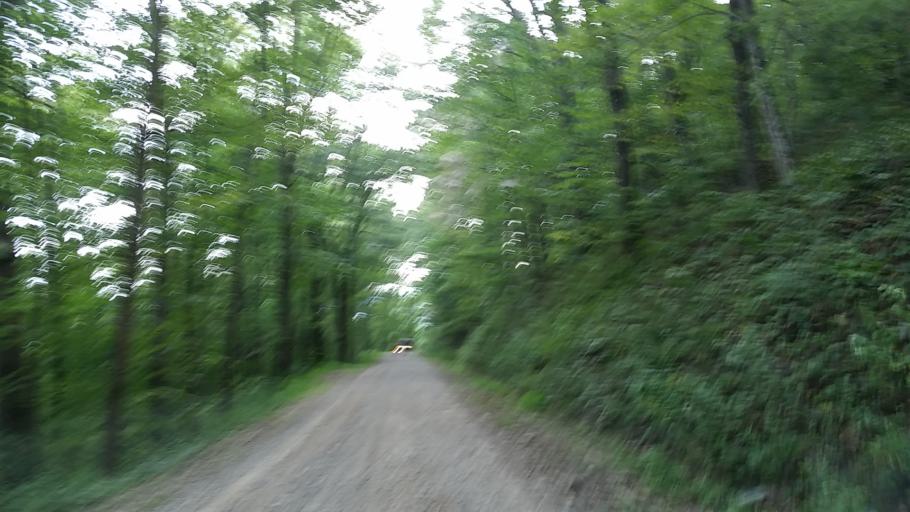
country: US
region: Georgia
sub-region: Lumpkin County
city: Dahlonega
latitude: 34.6495
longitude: -84.0714
